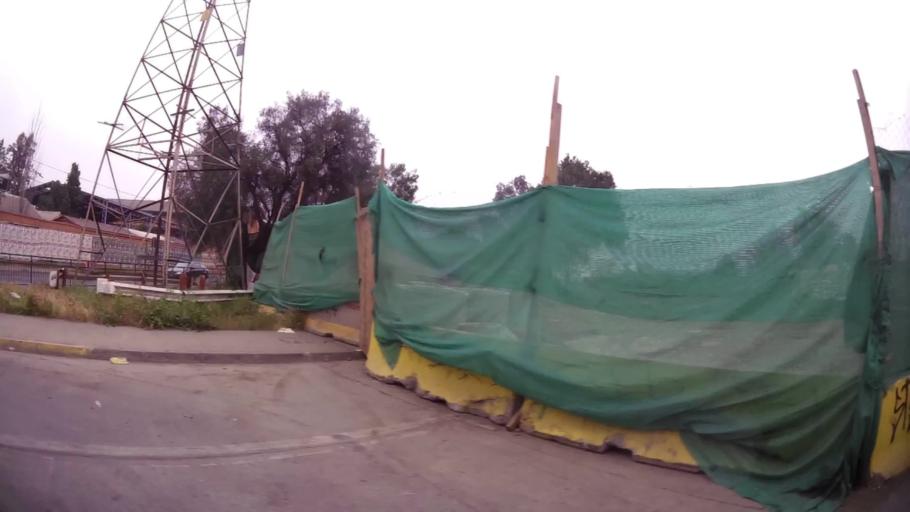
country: CL
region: Santiago Metropolitan
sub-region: Provincia de Santiago
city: Santiago
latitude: -33.4789
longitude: -70.6367
